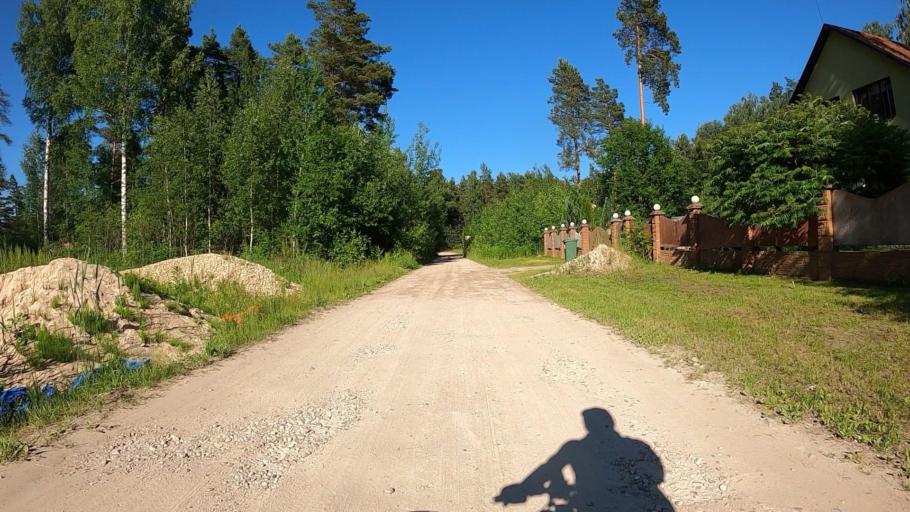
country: LV
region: Stopini
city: Ulbroka
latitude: 56.8776
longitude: 24.2983
